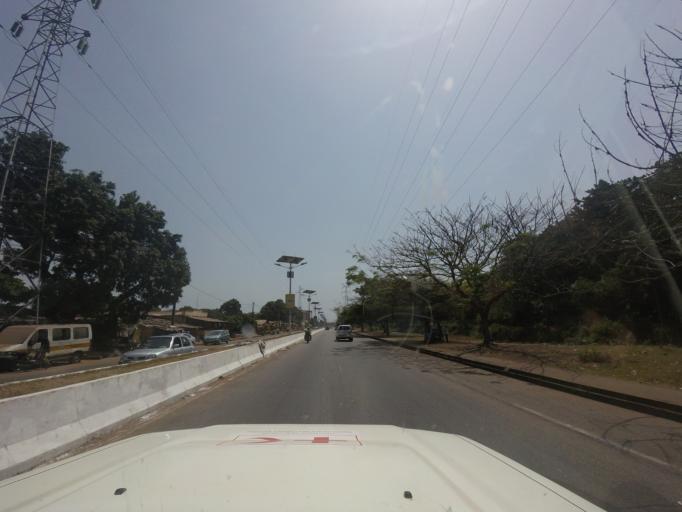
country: GN
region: Conakry
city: Camayenne
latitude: 9.5304
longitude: -13.6843
